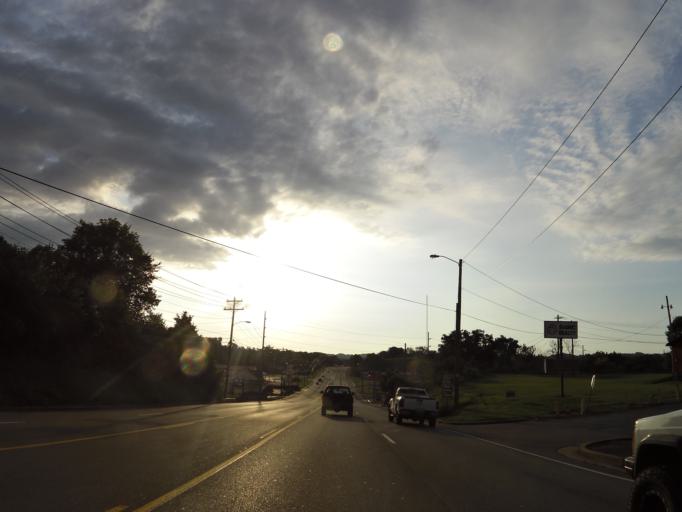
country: US
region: Tennessee
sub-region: Cocke County
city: Newport
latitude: 35.9708
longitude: -83.2086
